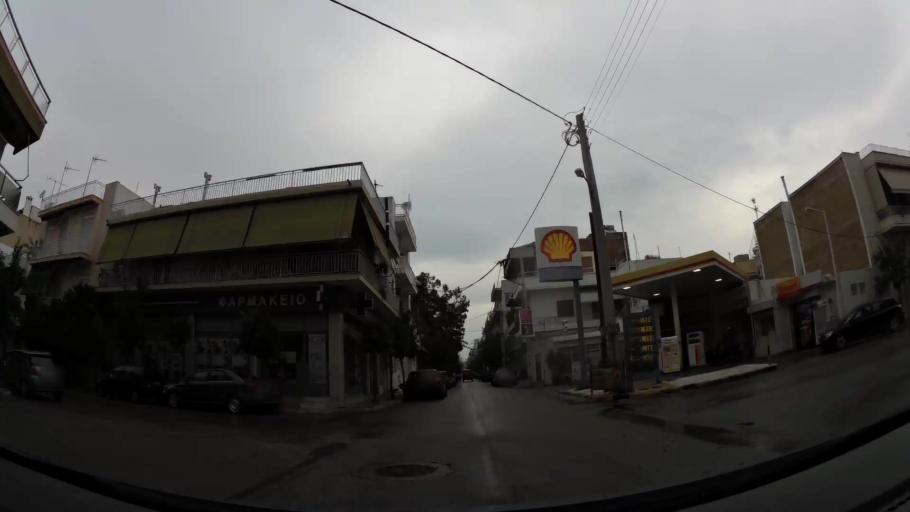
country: GR
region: Attica
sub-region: Nomarchia Athinas
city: Ymittos
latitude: 37.9559
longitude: 23.7511
